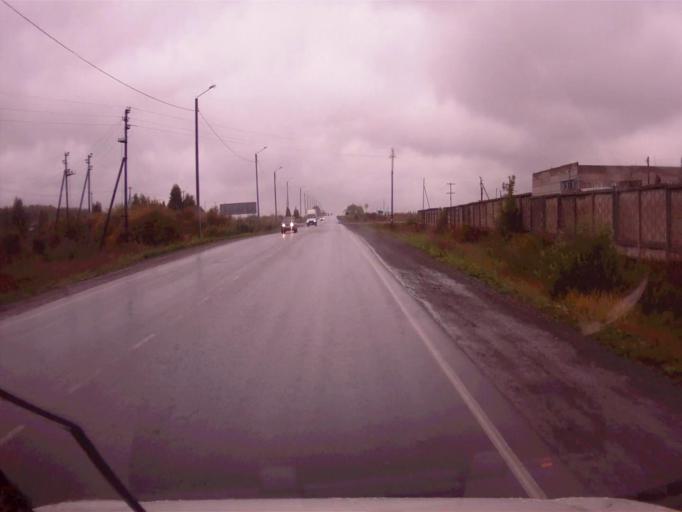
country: RU
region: Chelyabinsk
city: Argayash
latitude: 55.4773
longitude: 60.8629
